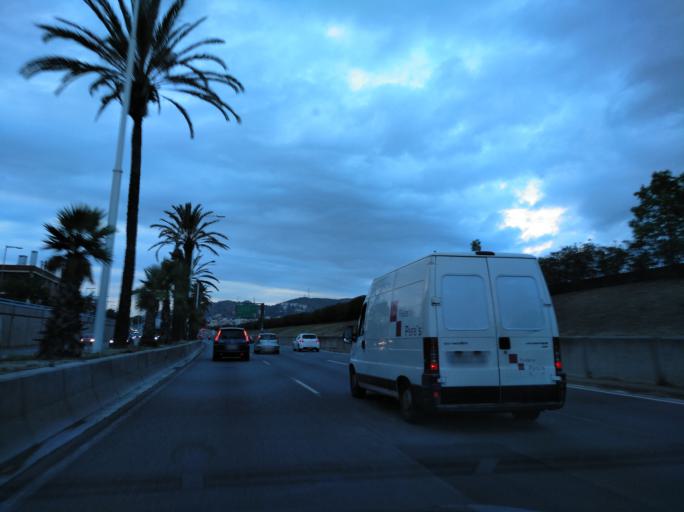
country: ES
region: Catalonia
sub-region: Provincia de Barcelona
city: Santa Coloma de Gramenet
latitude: 41.4404
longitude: 2.2080
